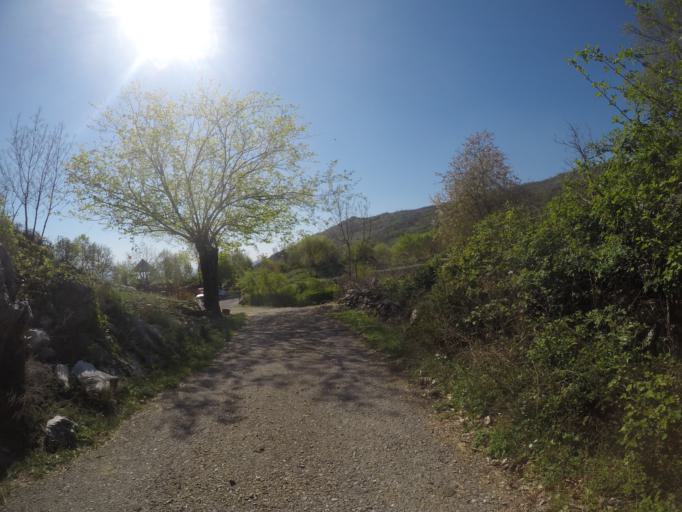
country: ME
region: Danilovgrad
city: Danilovgrad
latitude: 42.5168
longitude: 19.0568
